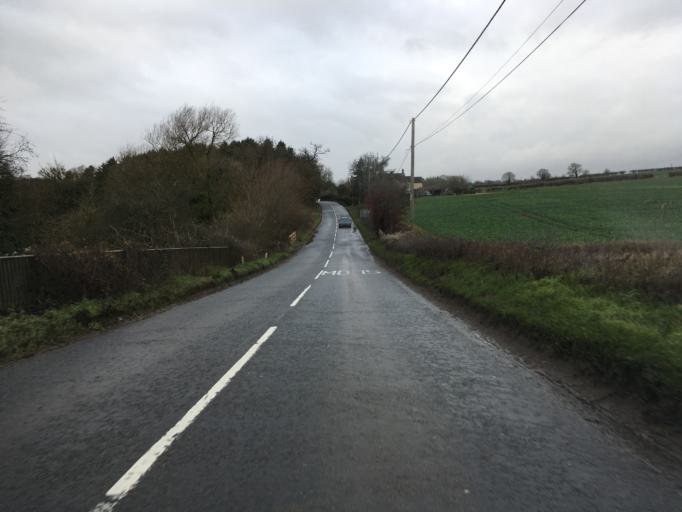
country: GB
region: England
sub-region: Wiltshire
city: Malmesbury
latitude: 51.6102
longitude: -2.1162
